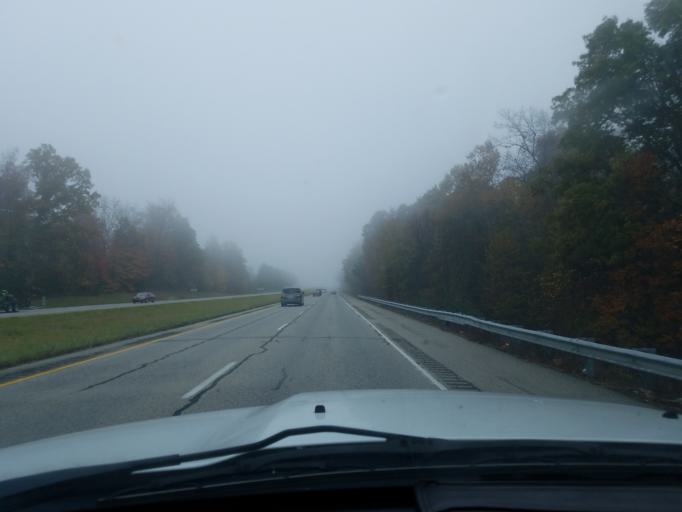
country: US
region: Indiana
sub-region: Floyd County
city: Galena
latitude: 38.3245
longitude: -85.8983
